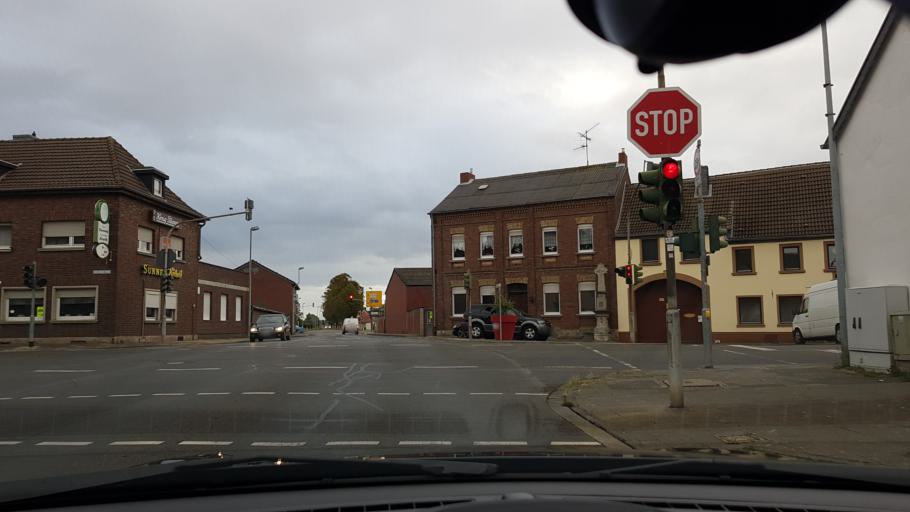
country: DE
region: North Rhine-Westphalia
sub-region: Regierungsbezirk Koln
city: Elsdorf
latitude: 50.9346
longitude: 6.5723
